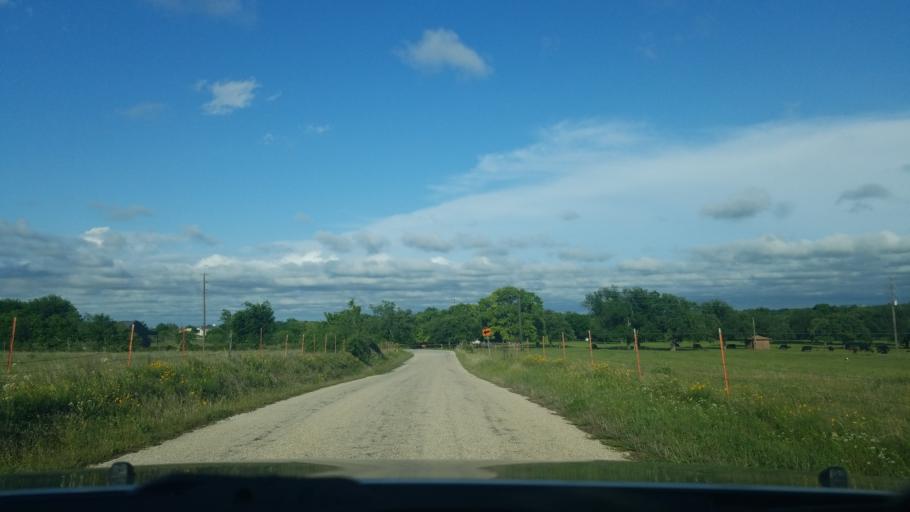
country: US
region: Texas
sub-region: Wise County
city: Decatur
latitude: 33.2427
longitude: -97.4834
